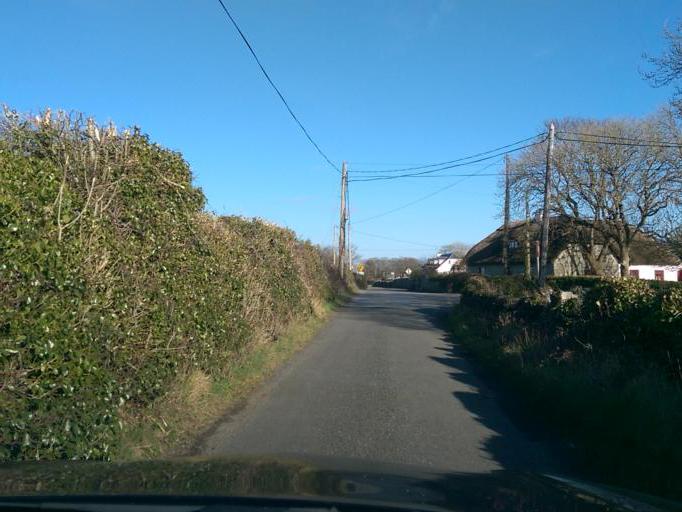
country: IE
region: Connaught
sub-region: County Galway
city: Oranmore
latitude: 53.2330
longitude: -8.9592
